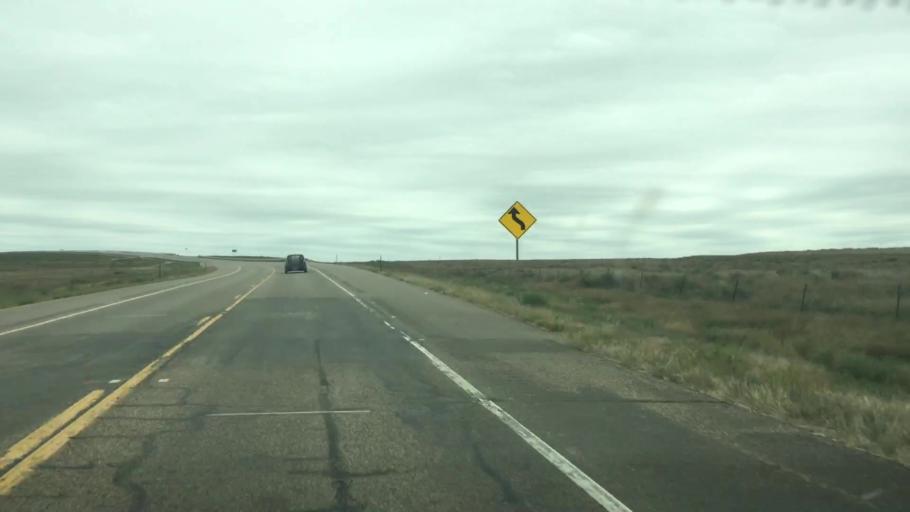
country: US
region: Colorado
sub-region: Prowers County
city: Lamar
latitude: 38.0510
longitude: -102.2637
